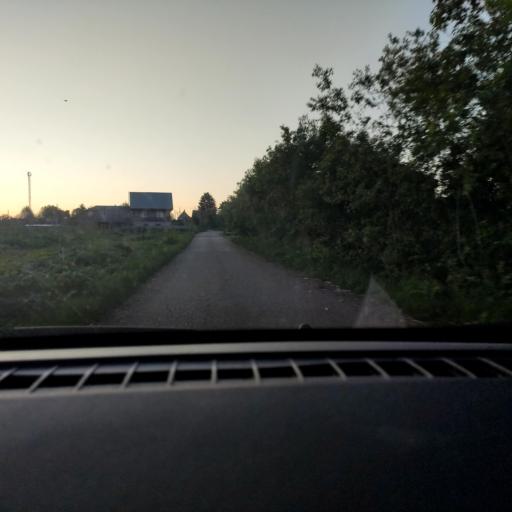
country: RU
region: Perm
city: Ferma
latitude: 57.9853
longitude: 56.3784
